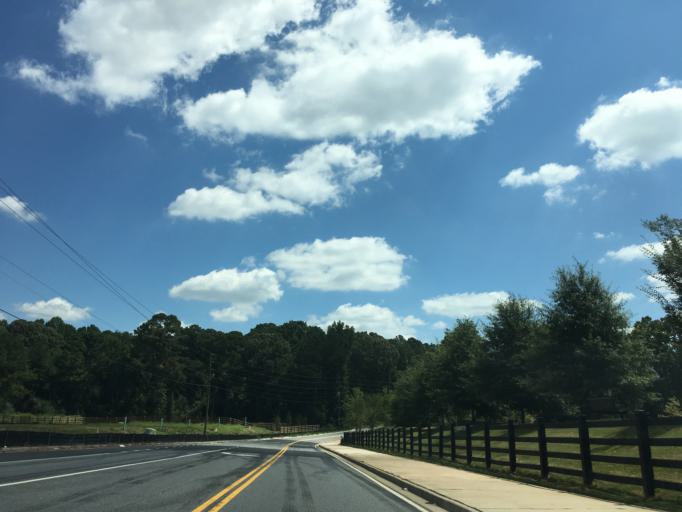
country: US
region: Georgia
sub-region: Fulton County
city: Milton
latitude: 34.1199
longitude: -84.2741
